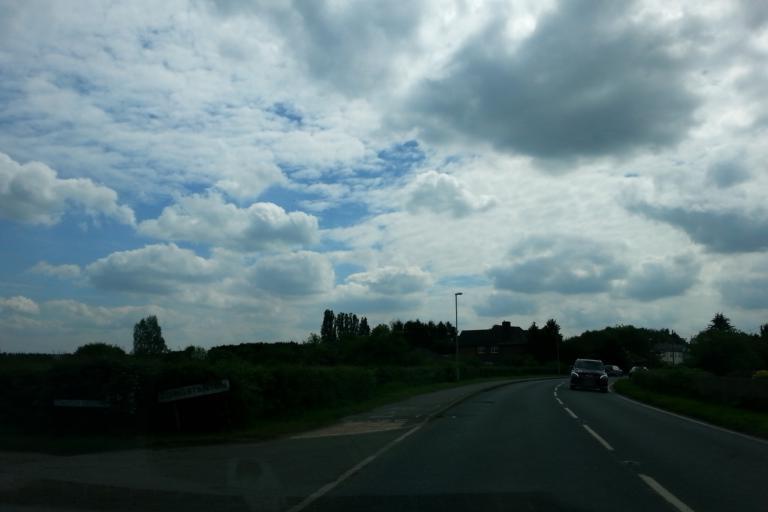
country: GB
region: England
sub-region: Cambridgeshire
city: Swavesey
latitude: 52.2996
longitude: 0.0514
